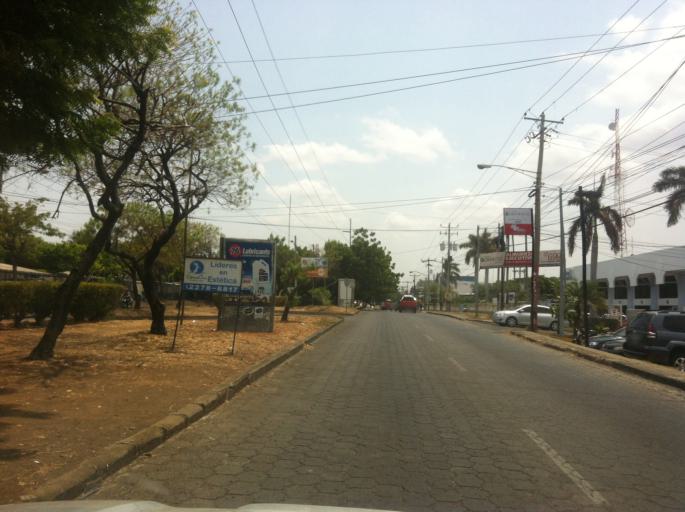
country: NI
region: Managua
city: Managua
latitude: 12.1128
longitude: -86.2584
